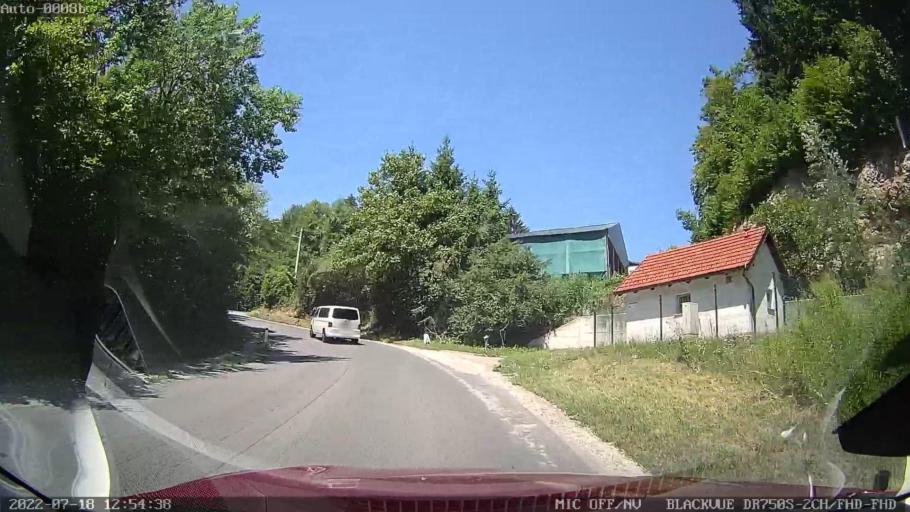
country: SI
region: Dobrova-Horjul-Polhov Gradec
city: Dobrova
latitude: 46.0759
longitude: 14.4404
